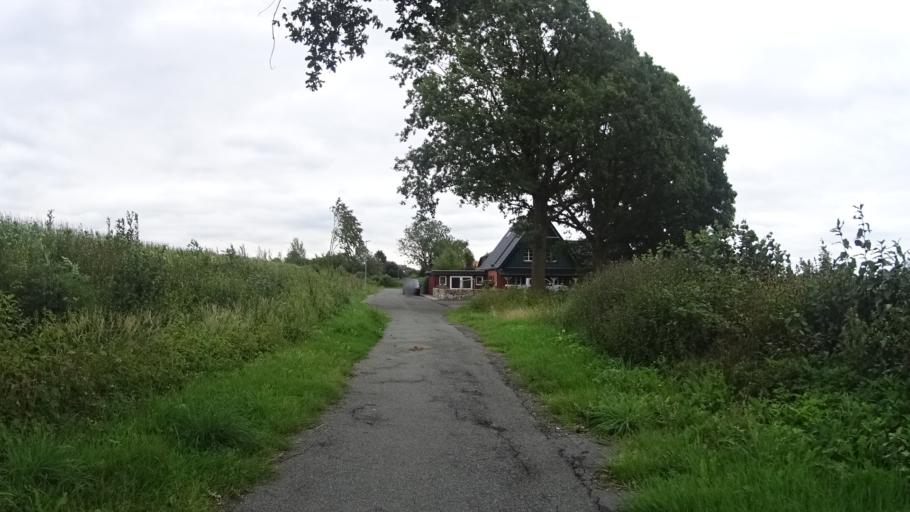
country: DE
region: Schleswig-Holstein
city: Jersbek
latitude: 53.7424
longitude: 10.2129
